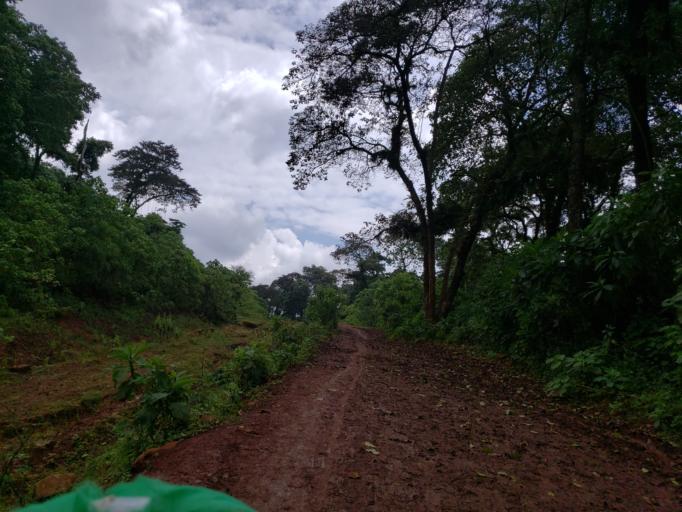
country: ET
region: Oromiya
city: Dodola
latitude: 6.4878
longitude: 39.4984
